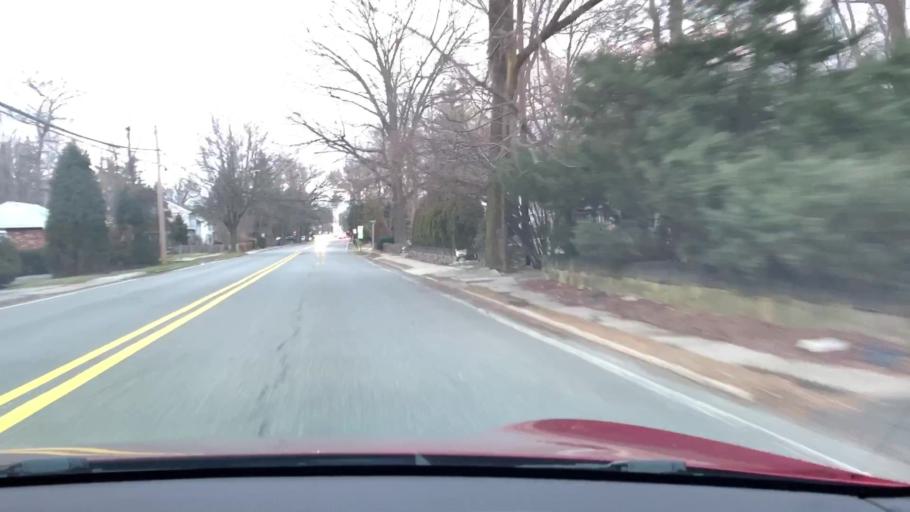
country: US
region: New Jersey
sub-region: Bergen County
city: Cresskill
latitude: 40.9378
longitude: -73.9772
